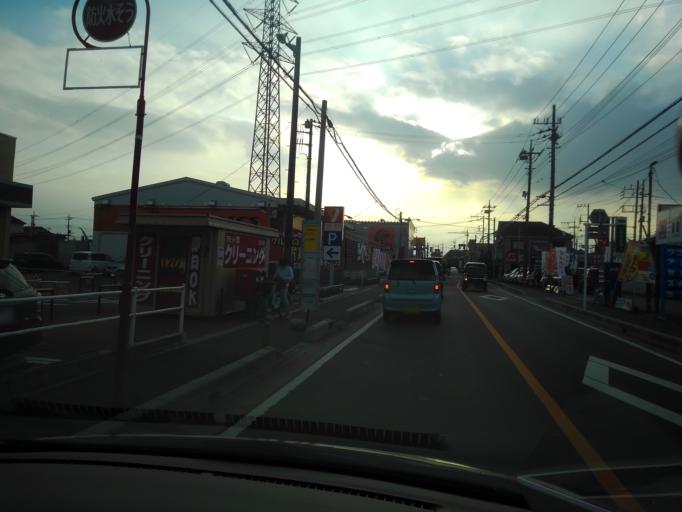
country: JP
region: Saitama
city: Tokorozawa
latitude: 35.7910
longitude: 139.4952
